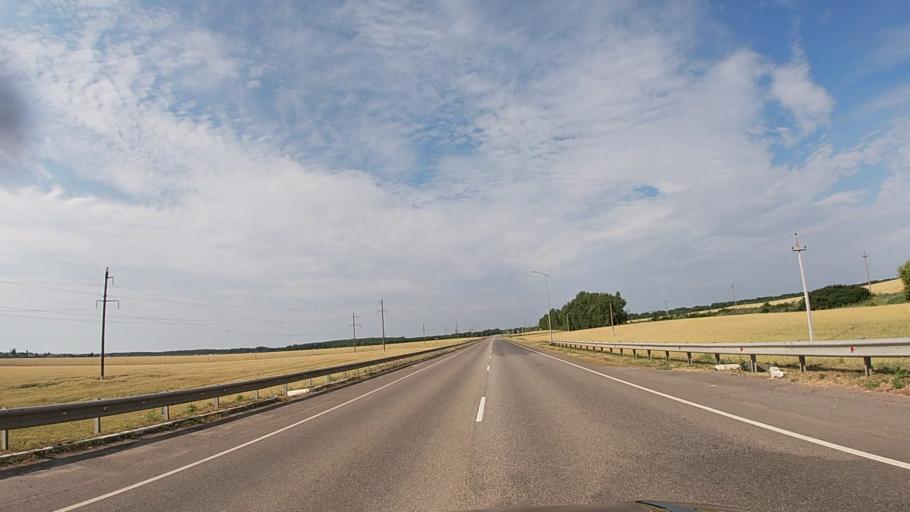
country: RU
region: Belgorod
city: Proletarskiy
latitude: 50.8113
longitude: 35.7477
